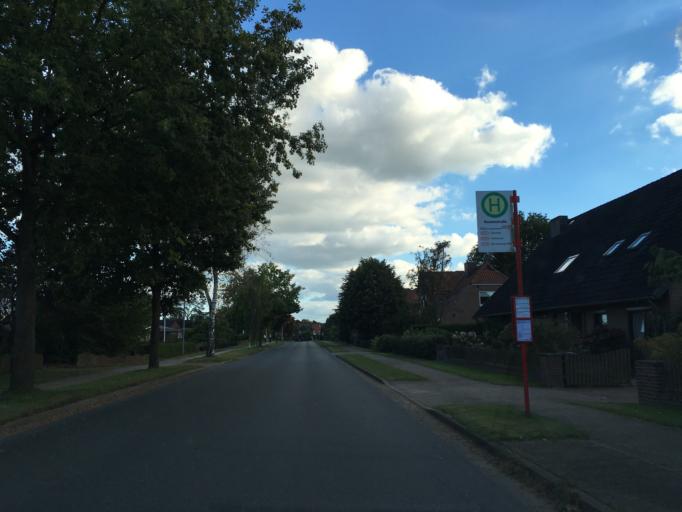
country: DE
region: Lower Saxony
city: Westergellersen
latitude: 53.2378
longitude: 10.2404
